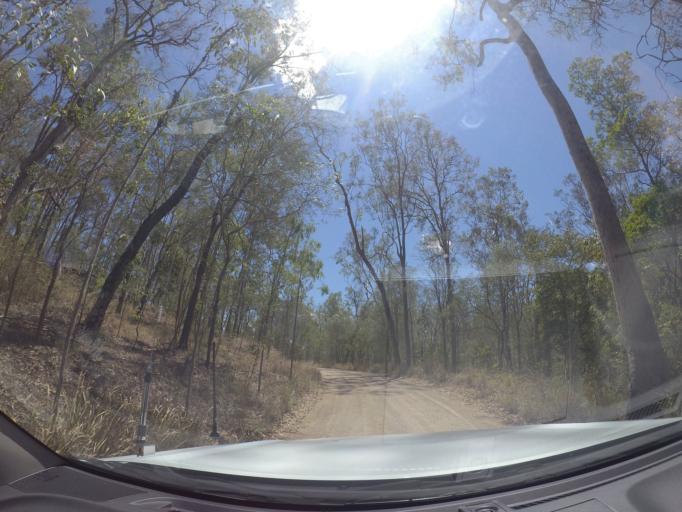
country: AU
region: Queensland
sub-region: Ipswich
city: Redbank Plains
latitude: -27.8043
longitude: 152.8437
